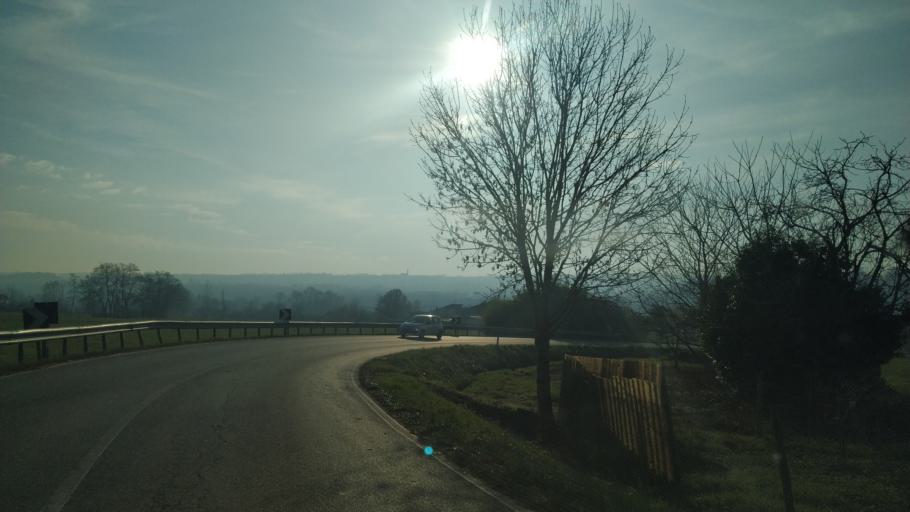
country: IT
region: Piedmont
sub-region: Provincia di Biella
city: Ceresane-Curanuova
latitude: 45.5257
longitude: 8.0136
